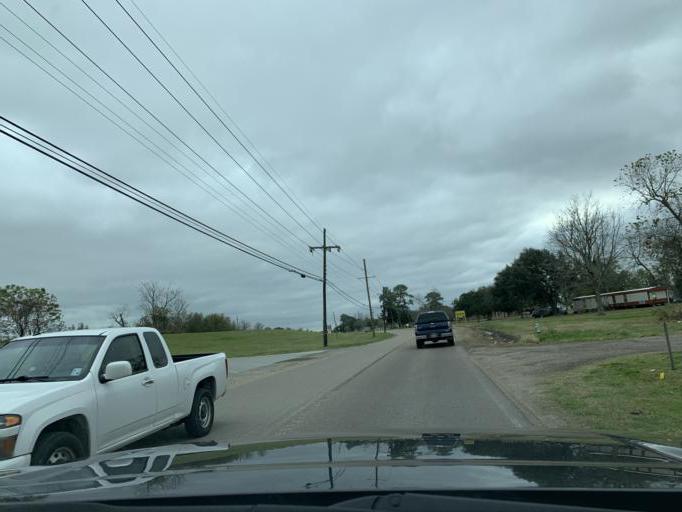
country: US
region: Louisiana
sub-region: Jefferson Parish
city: River Ridge
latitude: 29.9489
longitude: -90.2320
